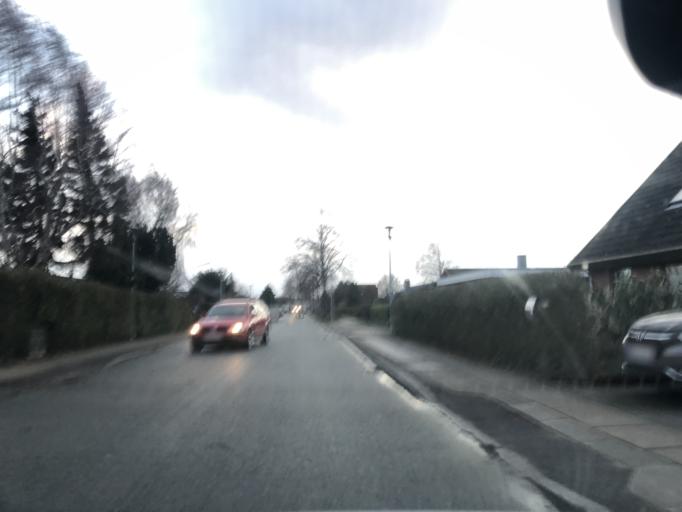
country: DK
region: Capital Region
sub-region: Tarnby Kommune
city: Tarnby
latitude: 55.6127
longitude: 12.5983
